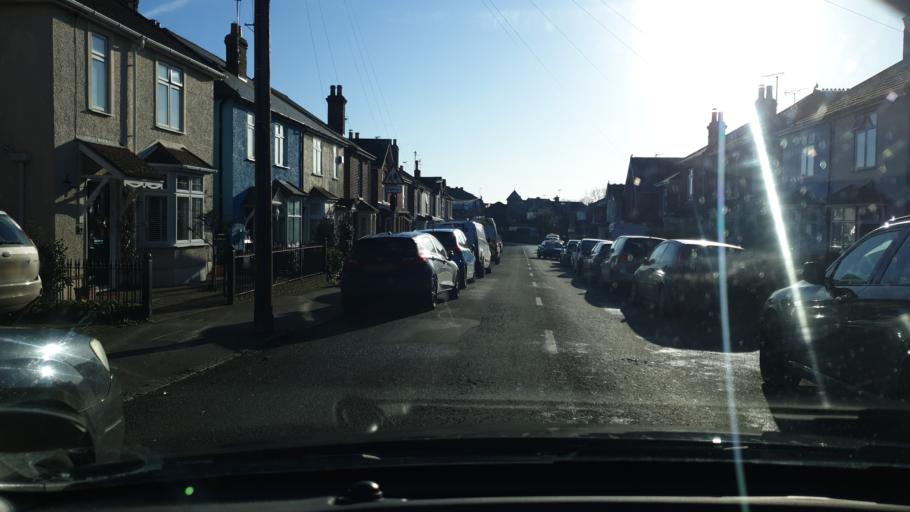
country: GB
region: England
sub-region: Essex
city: Brightlingsea
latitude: 51.8125
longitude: 1.0234
